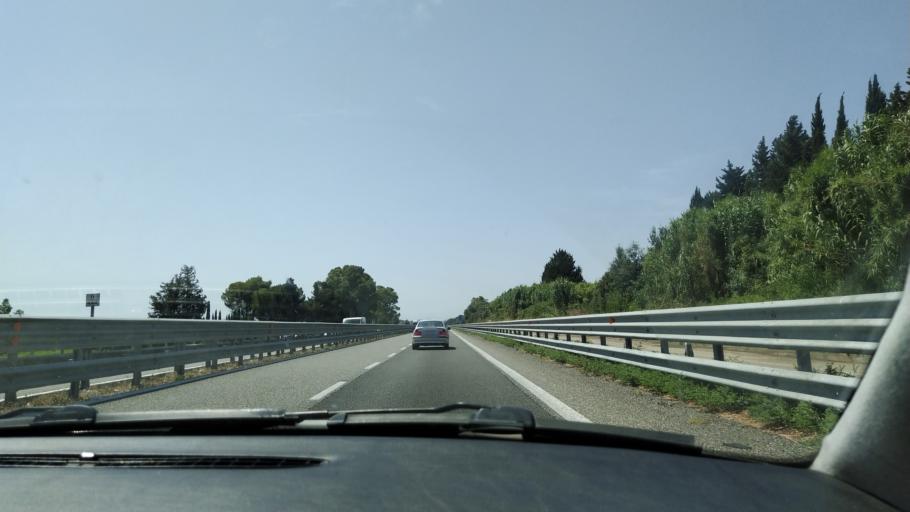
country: IT
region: Basilicate
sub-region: Provincia di Matera
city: Marconia
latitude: 40.3556
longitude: 16.7742
